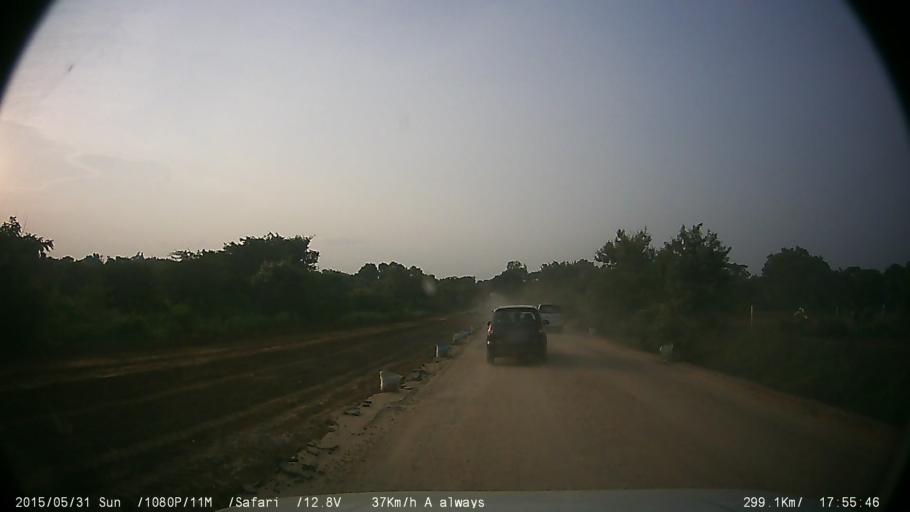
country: IN
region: Karnataka
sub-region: Mysore
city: Nanjangud
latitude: 11.9923
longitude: 76.6699
